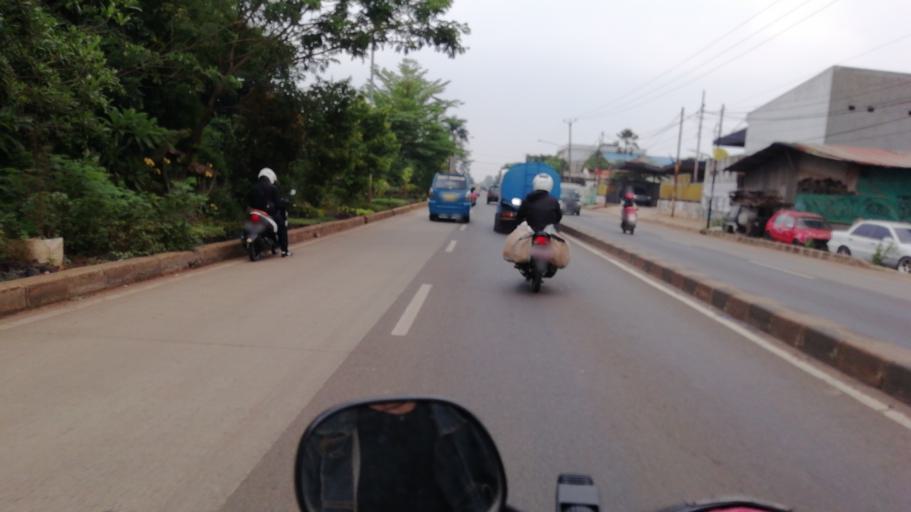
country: ID
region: West Java
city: Parung
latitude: -6.4566
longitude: 106.7308
